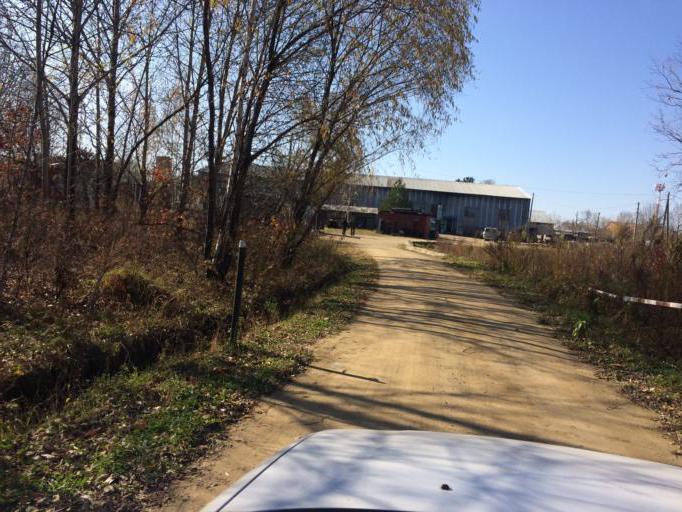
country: RU
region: Primorskiy
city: Dal'nerechensk
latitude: 45.9117
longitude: 133.8079
